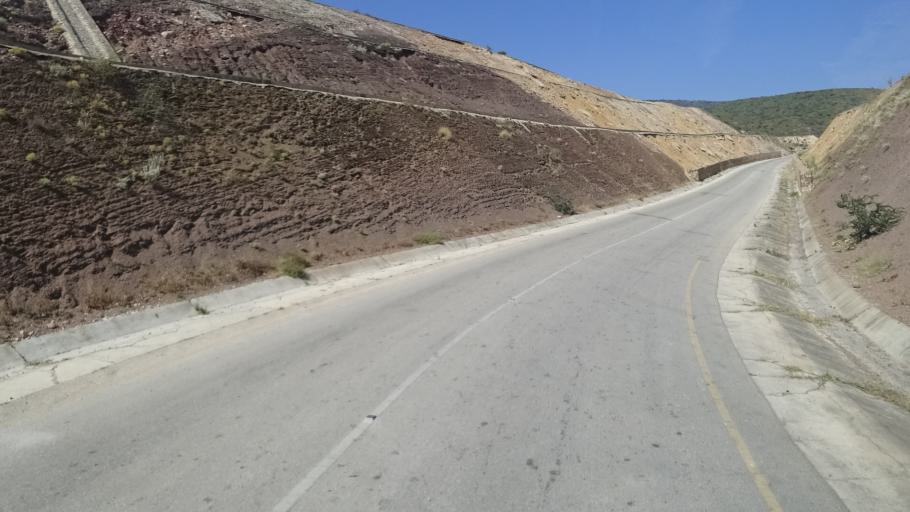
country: OM
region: Zufar
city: Salalah
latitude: 17.0468
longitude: 54.6115
